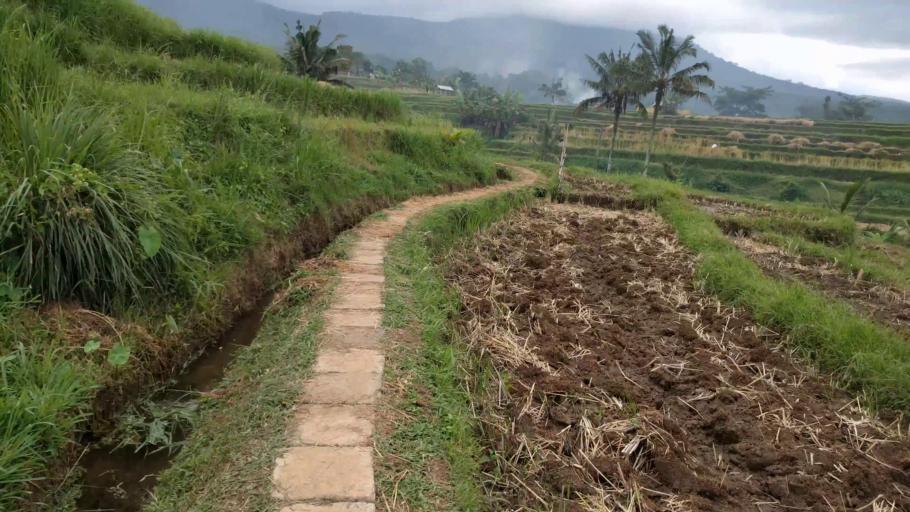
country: ID
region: Bali
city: Buahan Tengah
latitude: -8.5063
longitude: 115.1465
